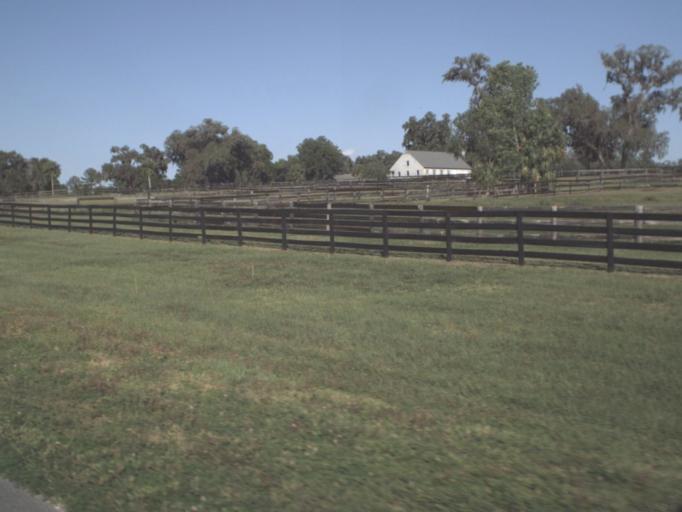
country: US
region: Florida
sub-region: Marion County
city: Dunnellon
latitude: 29.1600
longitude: -82.3486
